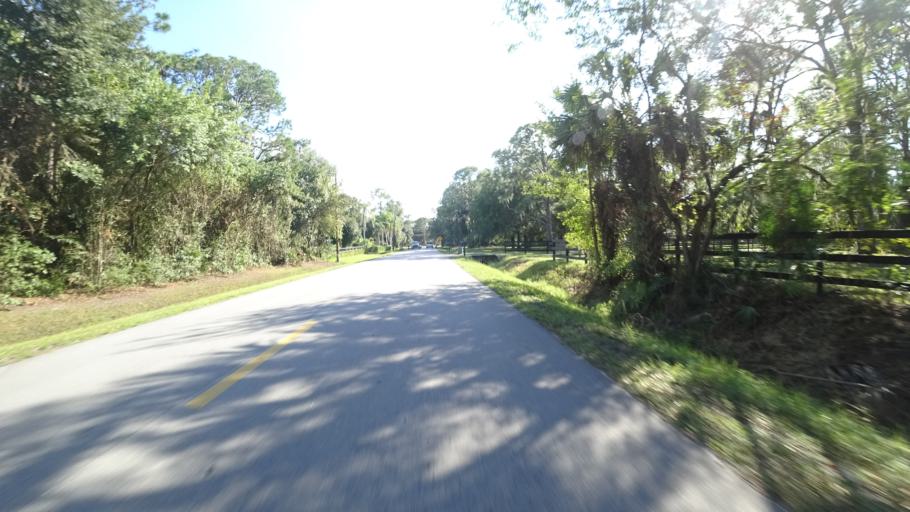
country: US
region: Florida
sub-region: Manatee County
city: Samoset
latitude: 27.4658
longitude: -82.4741
